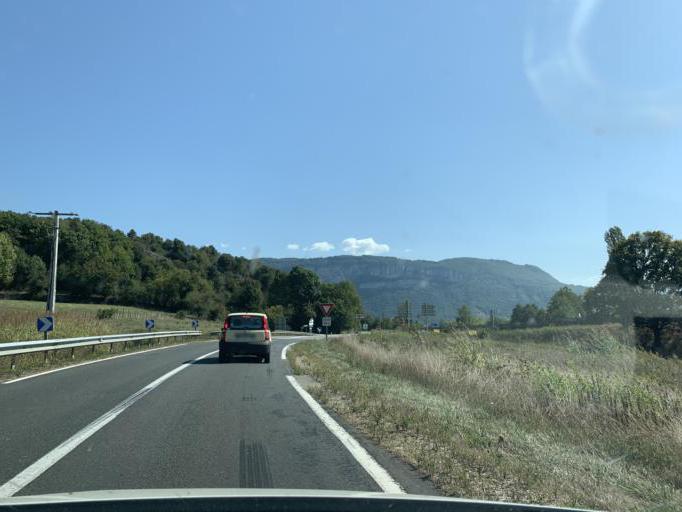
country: FR
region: Rhone-Alpes
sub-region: Departement de la Savoie
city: Saint-Genix-sur-Guiers
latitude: 45.6409
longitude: 5.6427
